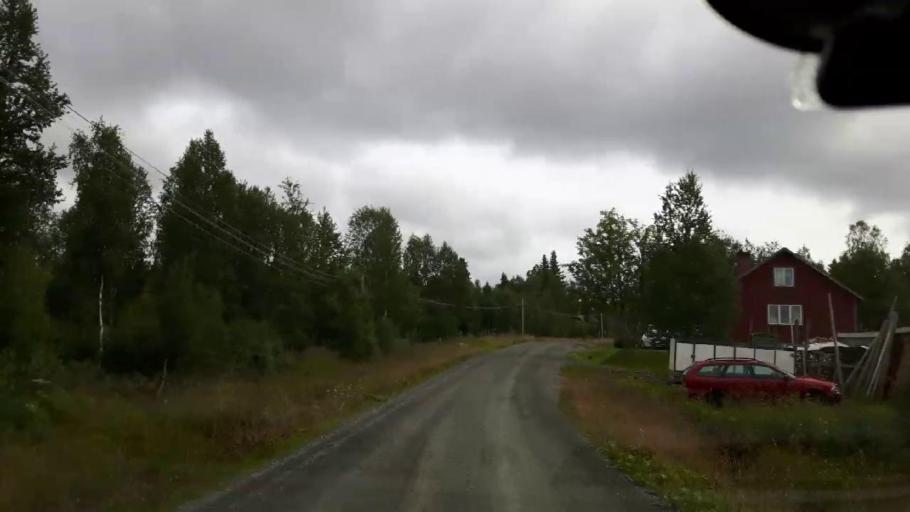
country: SE
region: Jaemtland
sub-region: Krokoms Kommun
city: Valla
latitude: 63.7803
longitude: 13.8240
